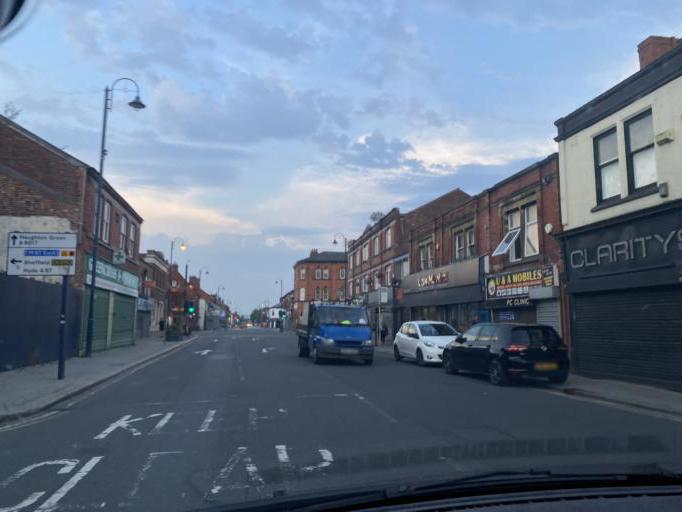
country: GB
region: England
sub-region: Borough of Tameside
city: Denton
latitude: 53.4569
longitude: -2.1141
